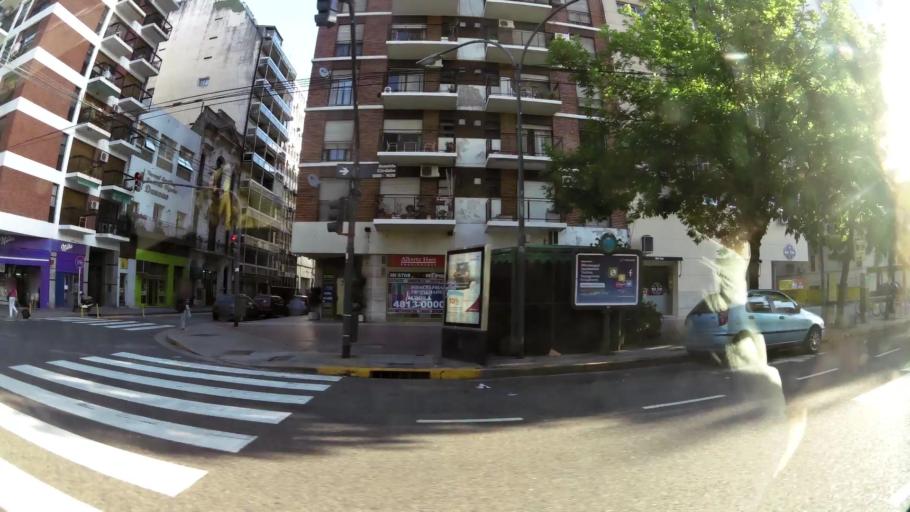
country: AR
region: Buenos Aires F.D.
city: Retiro
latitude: -34.5994
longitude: -58.3899
